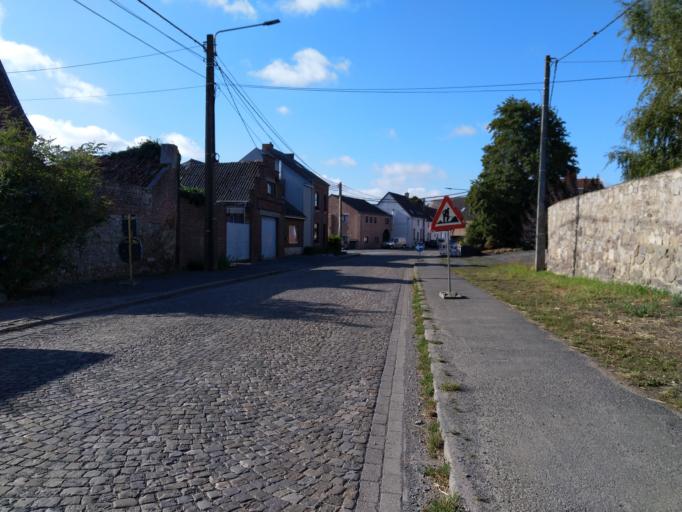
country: BE
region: Wallonia
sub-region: Province du Hainaut
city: Estinnes-au-Val
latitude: 50.4103
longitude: 4.1039
